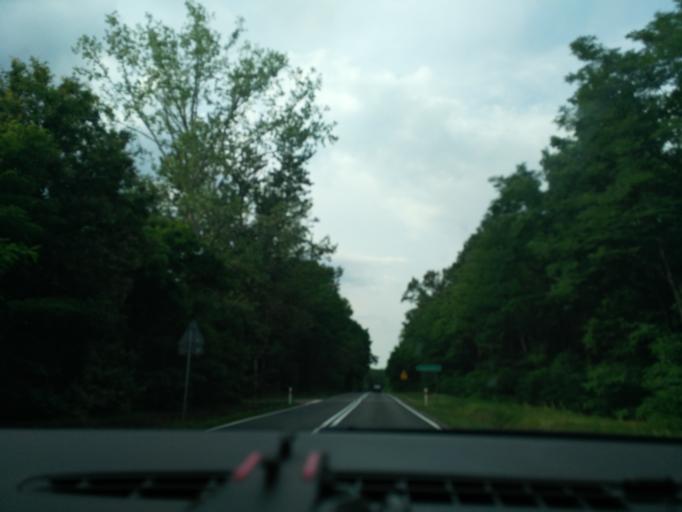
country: PL
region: Subcarpathian Voivodeship
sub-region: Powiat nizanski
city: Jezowe
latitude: 50.3977
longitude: 22.1303
